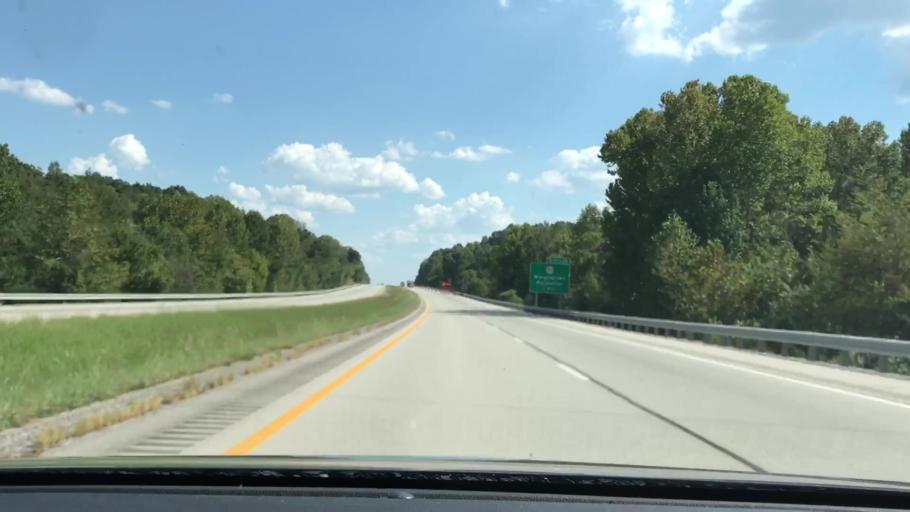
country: US
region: Kentucky
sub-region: Butler County
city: Morgantown
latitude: 37.2308
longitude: -86.7264
